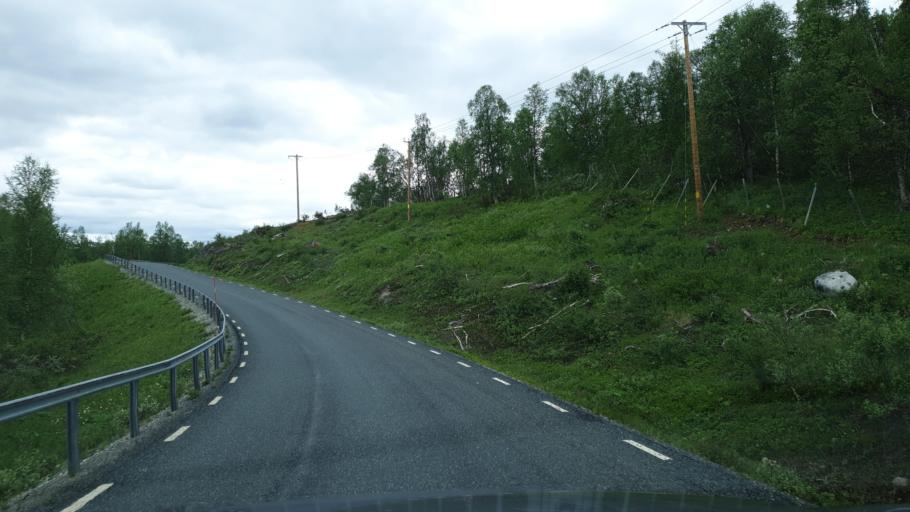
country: NO
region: Nordland
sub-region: Hattfjelldal
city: Hattfjelldal
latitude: 65.4179
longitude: 14.7908
